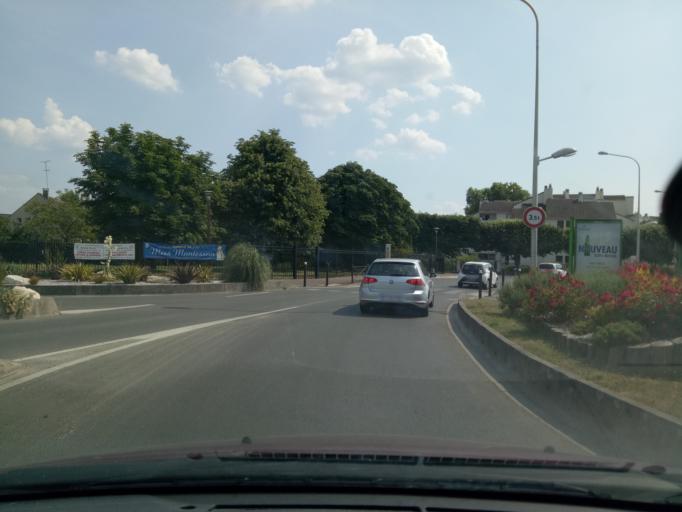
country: FR
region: Ile-de-France
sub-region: Departement des Yvelines
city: Montesson
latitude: 48.9120
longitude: 2.1464
